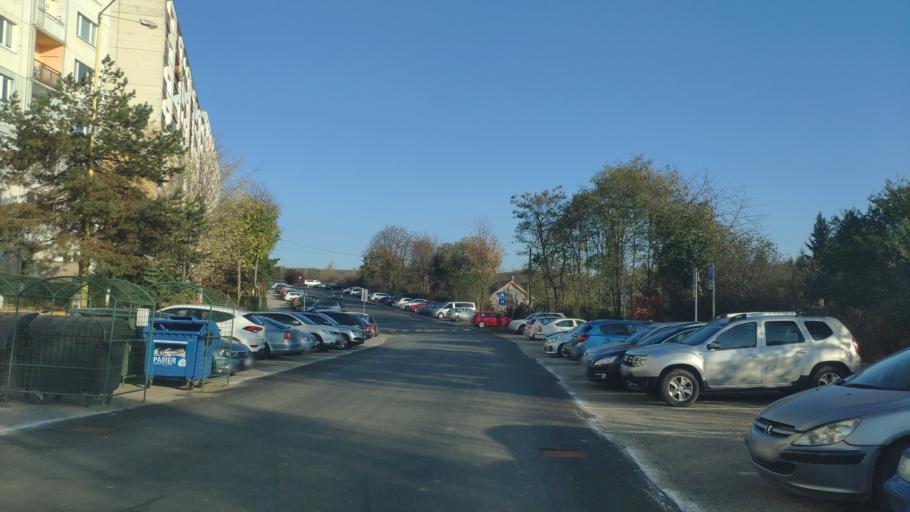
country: SK
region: Kosicky
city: Kosice
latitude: 48.7176
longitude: 21.2188
